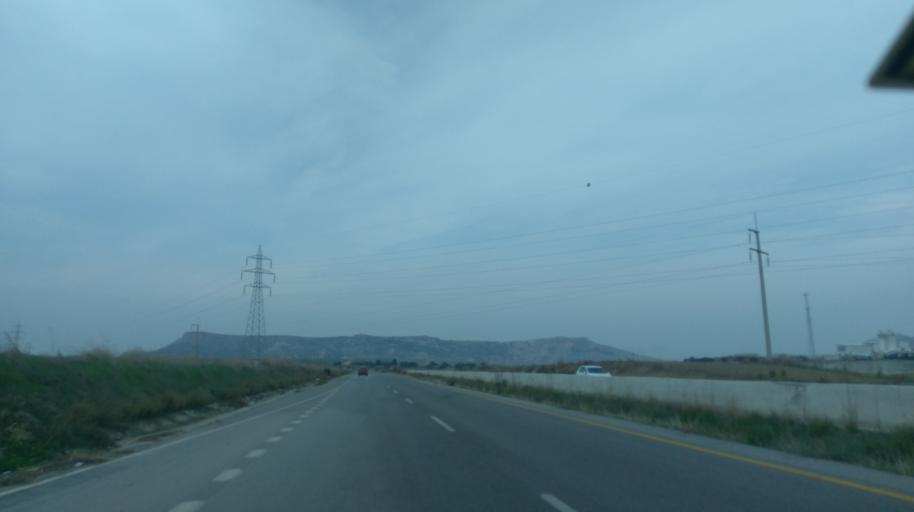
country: CY
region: Lefkosia
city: Mammari
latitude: 35.2213
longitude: 33.1615
